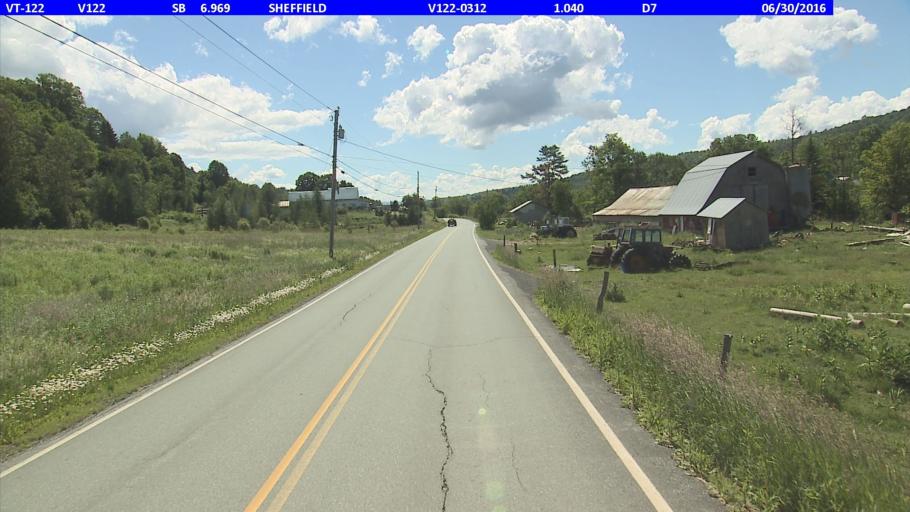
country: US
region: Vermont
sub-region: Caledonia County
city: Lyndonville
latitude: 44.5987
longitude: -72.1088
